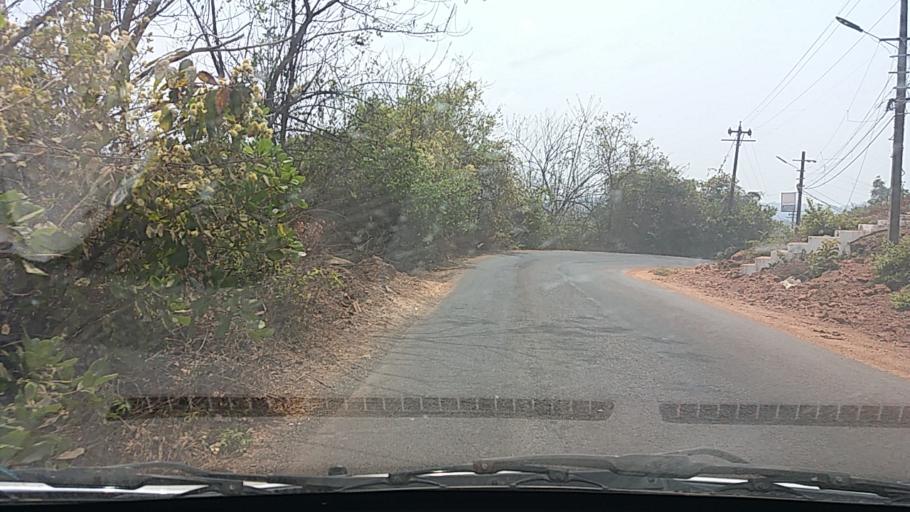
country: IN
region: Goa
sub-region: North Goa
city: Saligao
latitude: 15.5319
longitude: 73.7997
